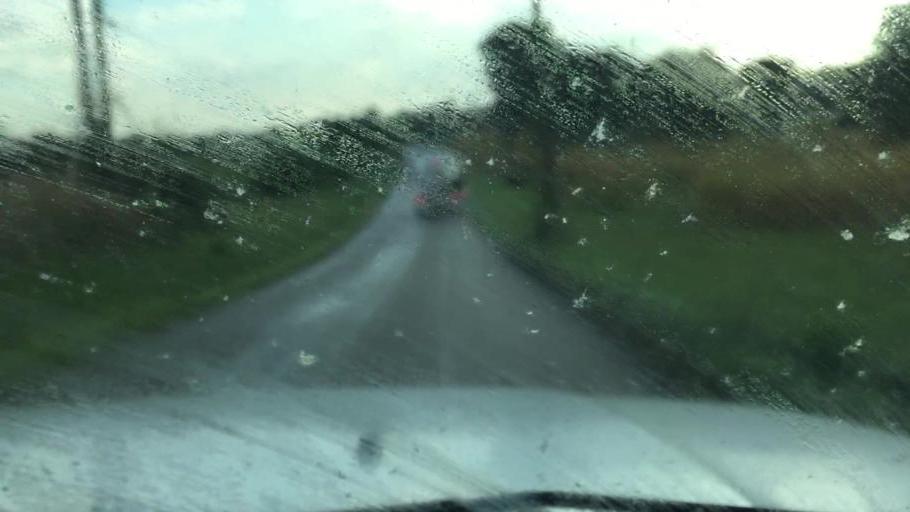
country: US
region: Ohio
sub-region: Champaign County
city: Mechanicsburg
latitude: 40.0291
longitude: -83.6104
